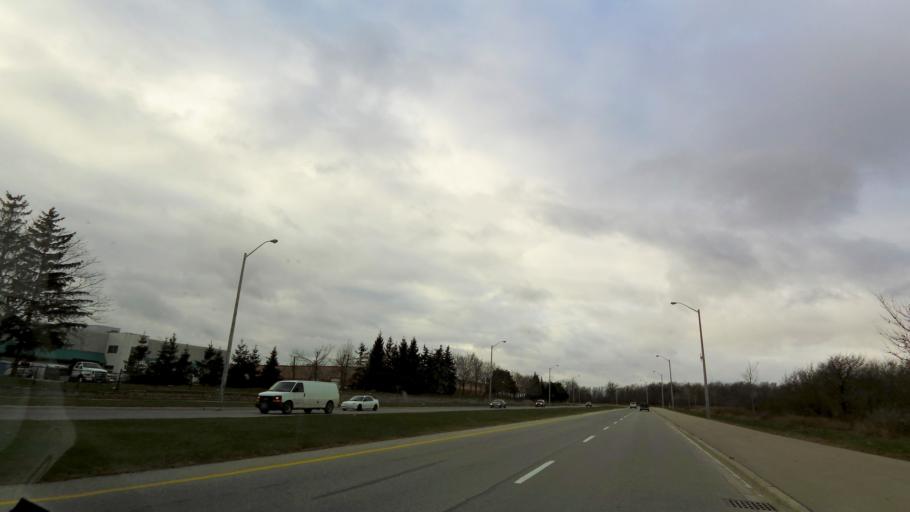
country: CA
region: Ontario
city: Brampton
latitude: 43.7629
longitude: -79.7015
